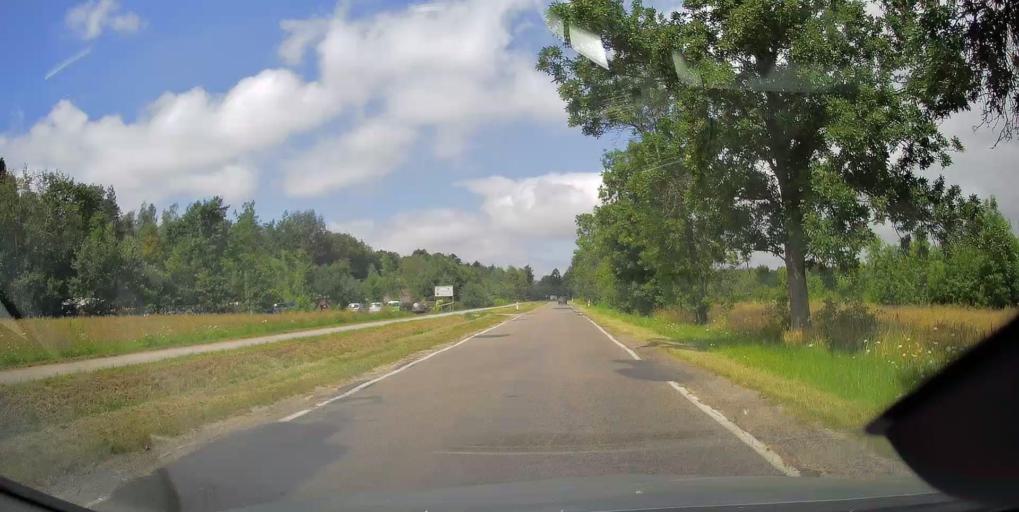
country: PL
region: Swietokrzyskie
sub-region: Powiat opatowski
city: Iwaniska
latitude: 50.7056
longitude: 21.3268
